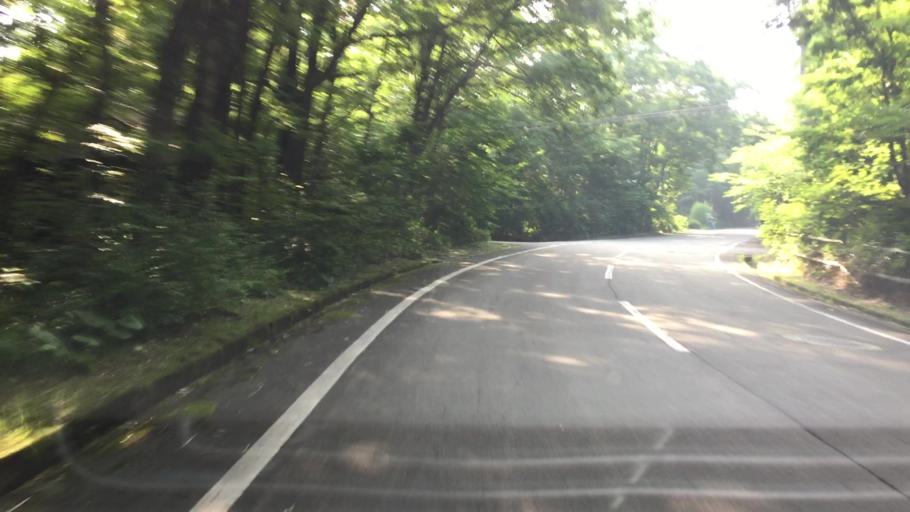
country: JP
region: Tochigi
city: Kuroiso
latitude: 37.1084
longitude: 140.0385
